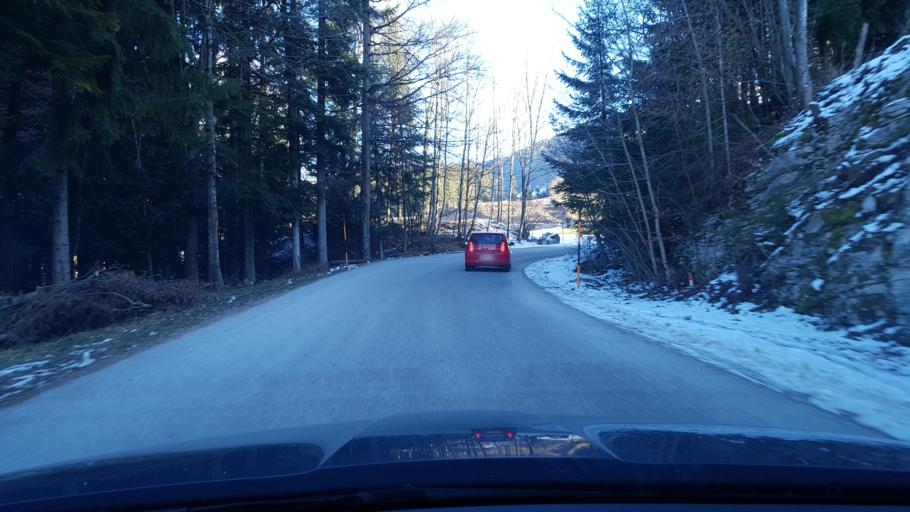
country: AT
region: Salzburg
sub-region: Politischer Bezirk Hallein
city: Kuchl
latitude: 47.6593
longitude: 13.1823
